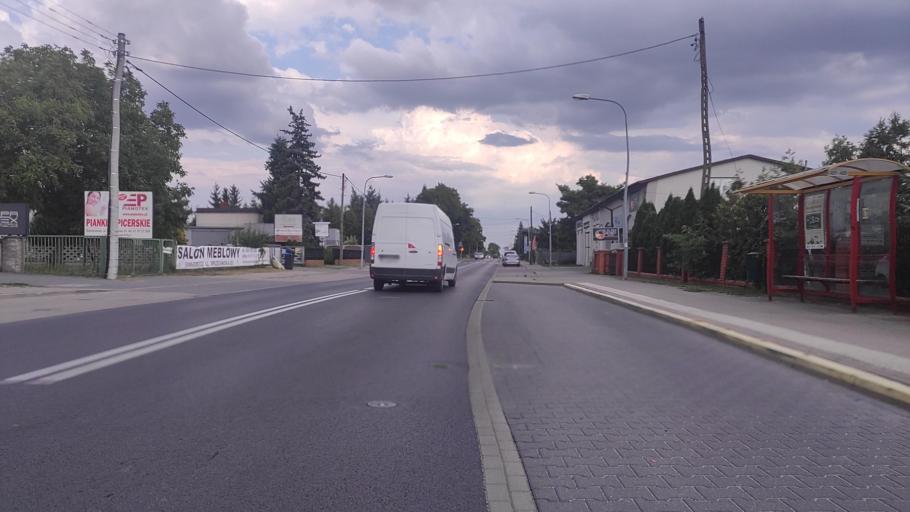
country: PL
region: Greater Poland Voivodeship
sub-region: Powiat poznanski
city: Swarzedz
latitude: 52.4088
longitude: 17.0934
